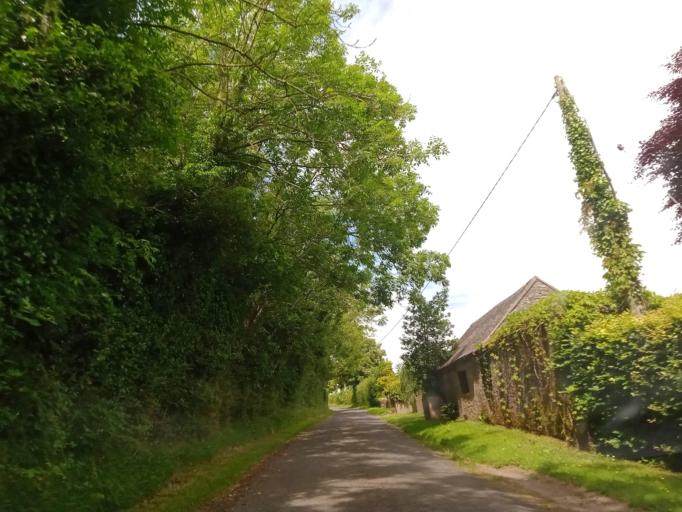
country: IE
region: Leinster
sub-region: Kilkenny
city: Thomastown
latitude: 52.5641
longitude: -7.1241
